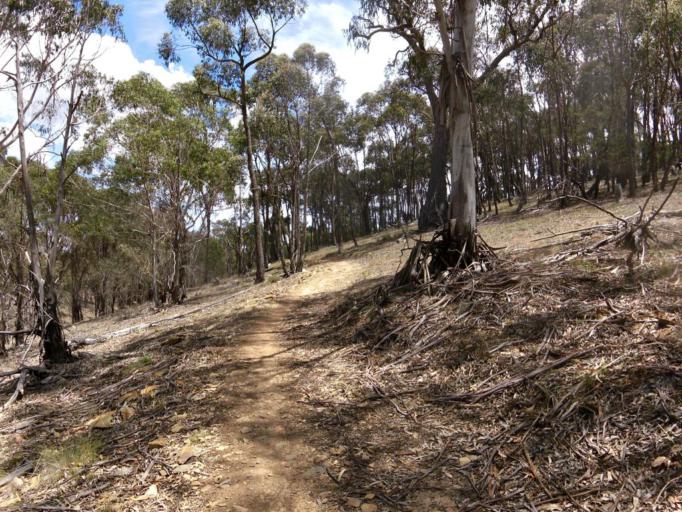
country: AU
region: Australian Capital Territory
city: Kaleen
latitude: -35.1371
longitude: 149.1434
